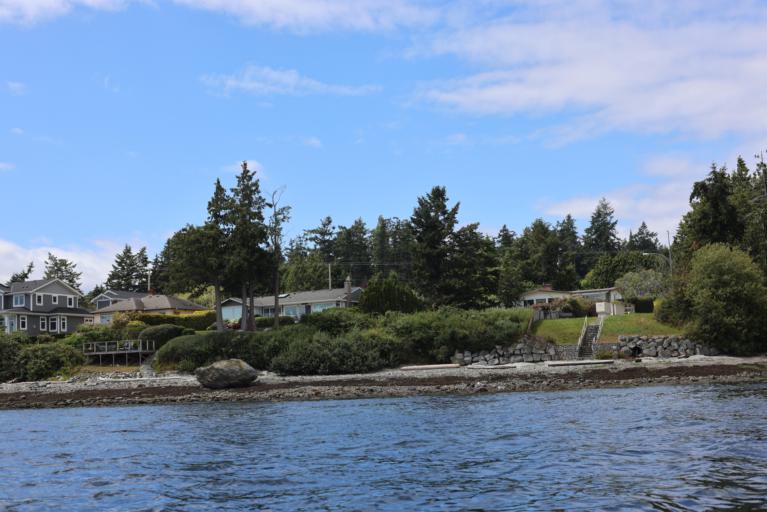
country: CA
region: British Columbia
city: North Saanich
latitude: 48.6158
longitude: -123.3993
